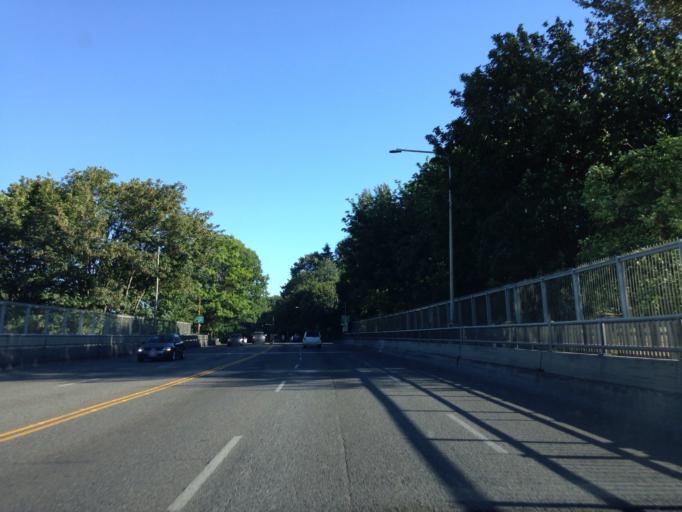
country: US
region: Washington
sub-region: King County
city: Seattle
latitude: 47.6440
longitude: -122.3473
